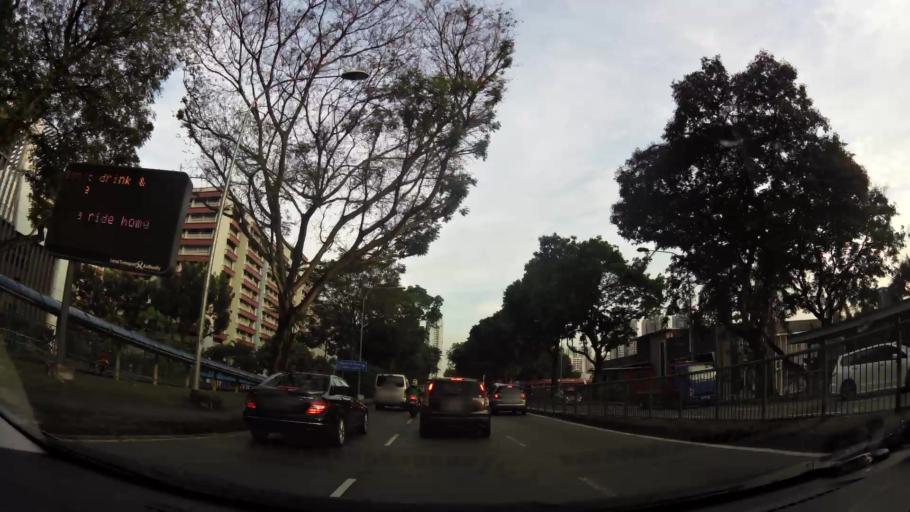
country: SG
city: Singapore
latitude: 1.3185
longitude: 103.8552
